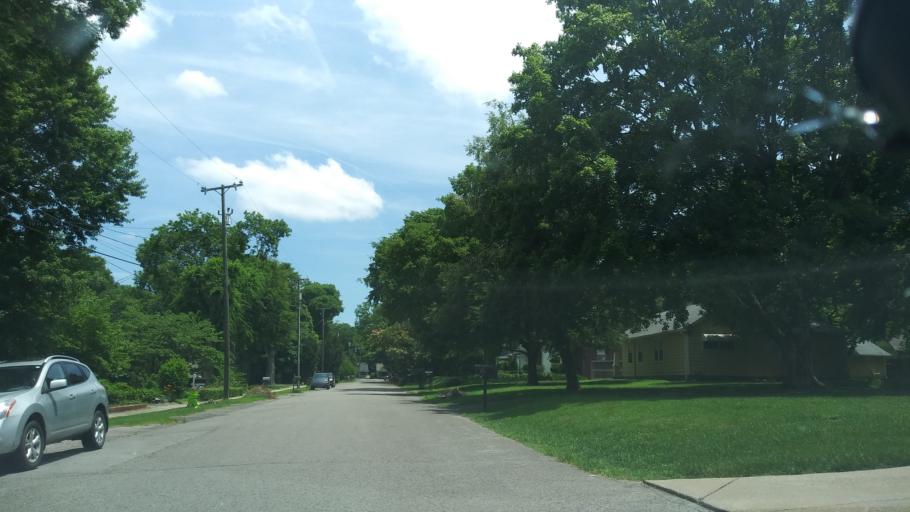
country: US
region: Tennessee
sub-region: Davidson County
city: Belle Meade
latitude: 36.1373
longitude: -86.8368
